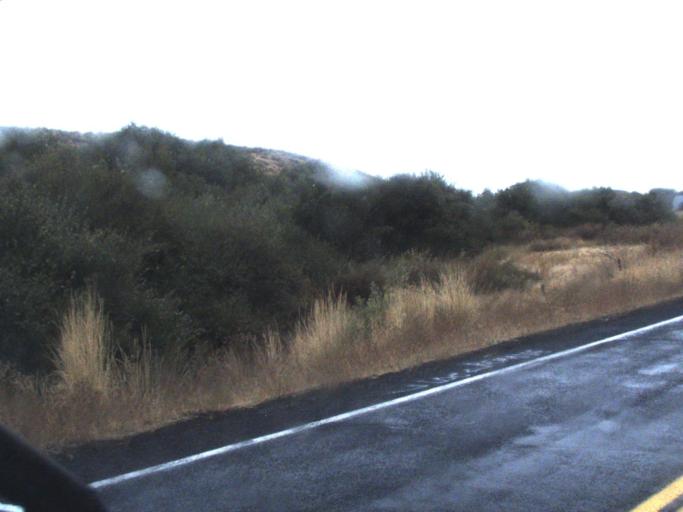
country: US
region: Washington
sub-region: Lincoln County
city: Davenport
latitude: 47.3505
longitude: -118.0975
